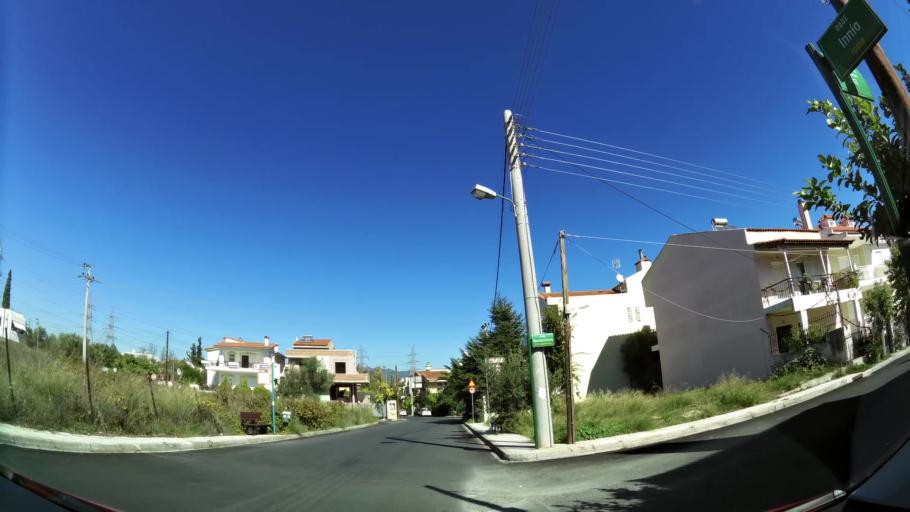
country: GR
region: Attica
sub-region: Nomarchia Anatolikis Attikis
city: Leondarion
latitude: 37.9911
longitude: 23.8592
